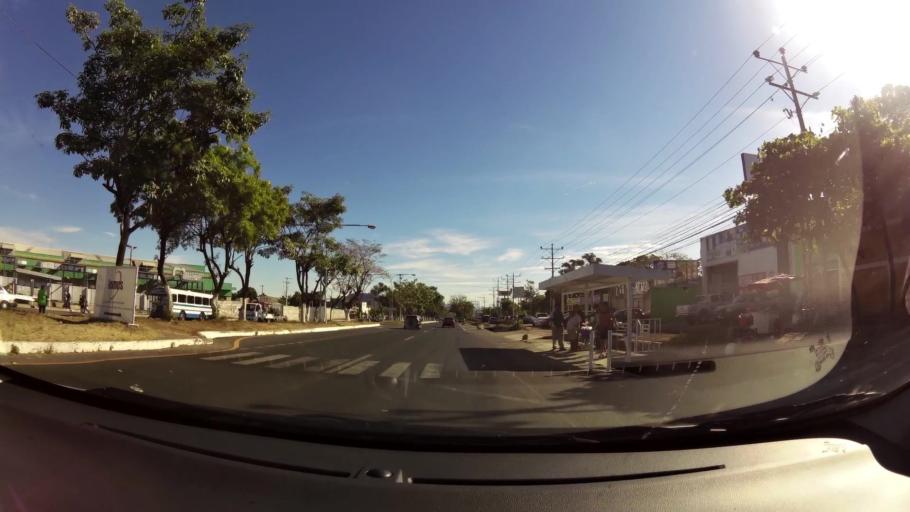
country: SV
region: Santa Ana
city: Santa Ana
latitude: 13.9767
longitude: -89.5597
